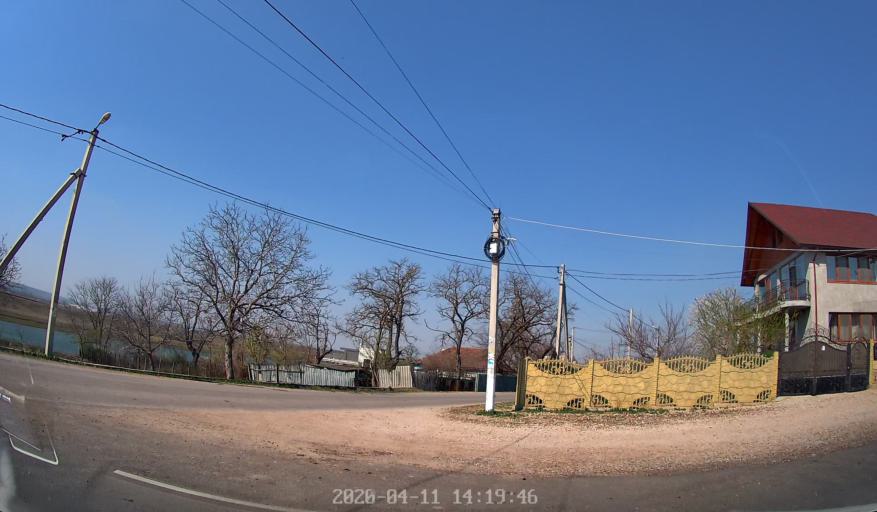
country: MD
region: Chisinau
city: Vadul lui Voda
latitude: 47.0842
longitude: 29.1309
